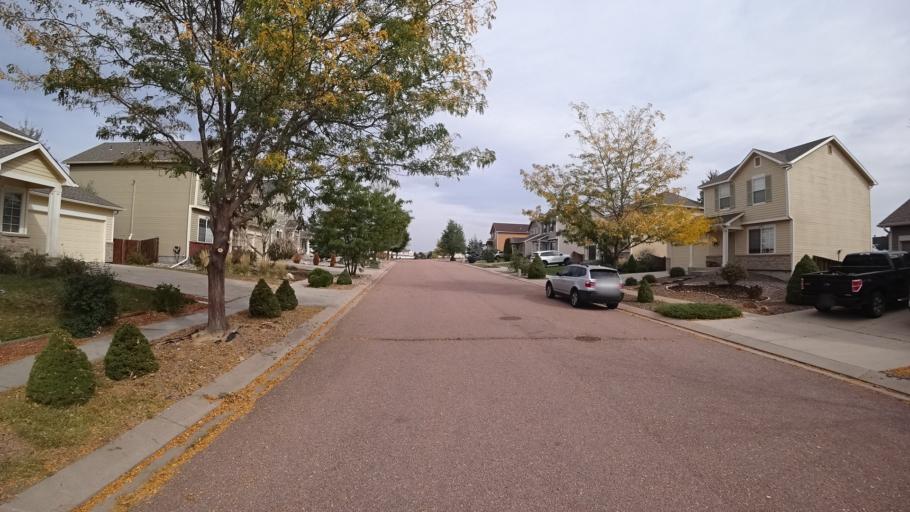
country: US
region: Colorado
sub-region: El Paso County
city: Cimarron Hills
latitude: 38.9230
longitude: -104.7143
